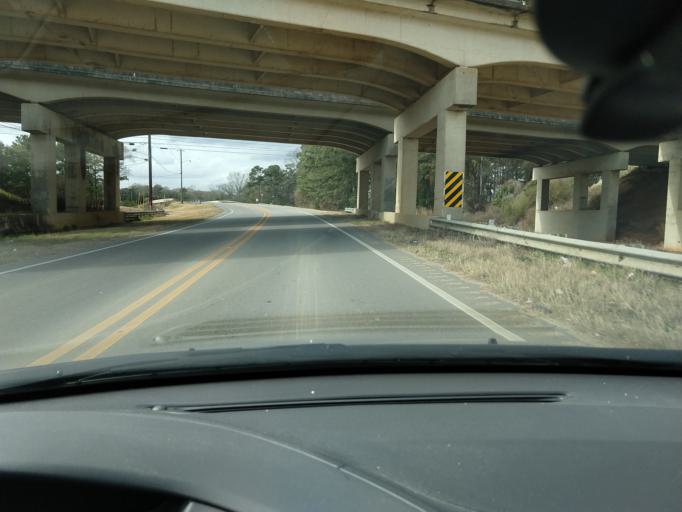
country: US
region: Alabama
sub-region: Houston County
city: Dothan
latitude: 31.2227
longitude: -85.3602
